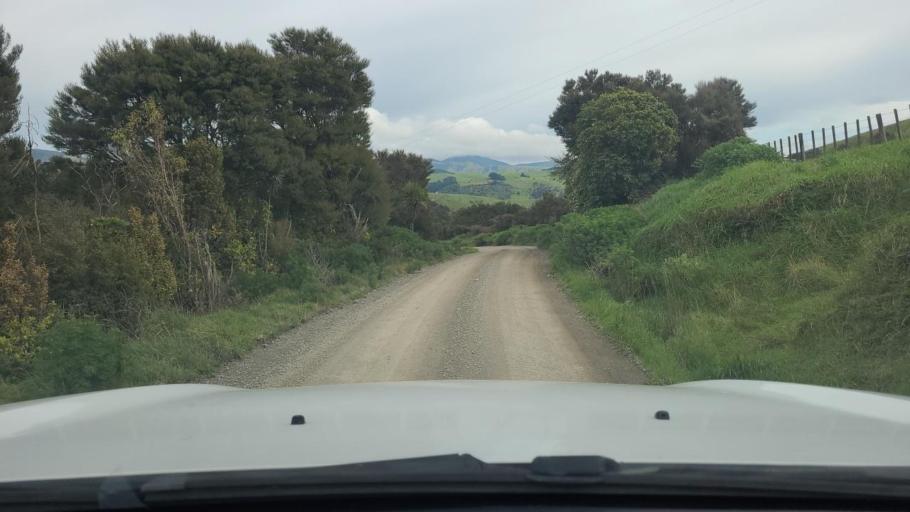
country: NZ
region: Wellington
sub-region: South Wairarapa District
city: Waipawa
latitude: -41.3659
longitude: 175.4839
